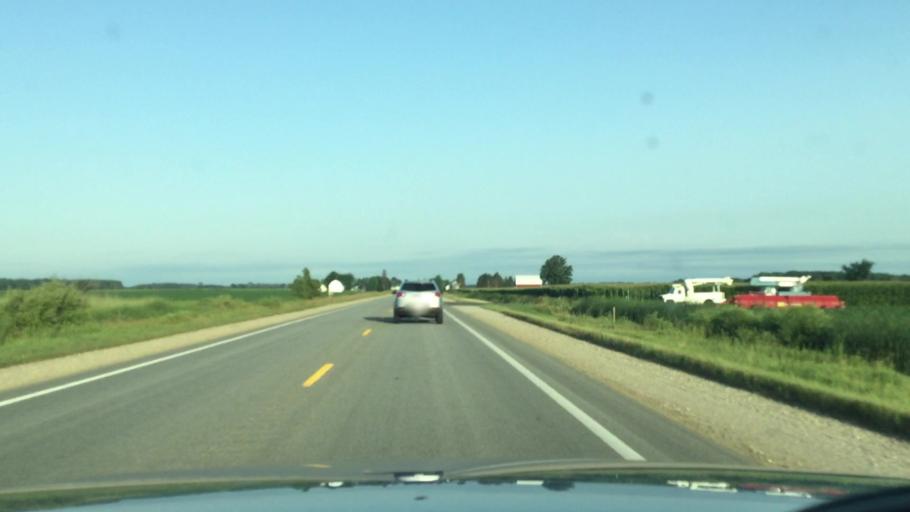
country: US
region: Michigan
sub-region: Montcalm County
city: Carson City
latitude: 43.1763
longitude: -84.7473
